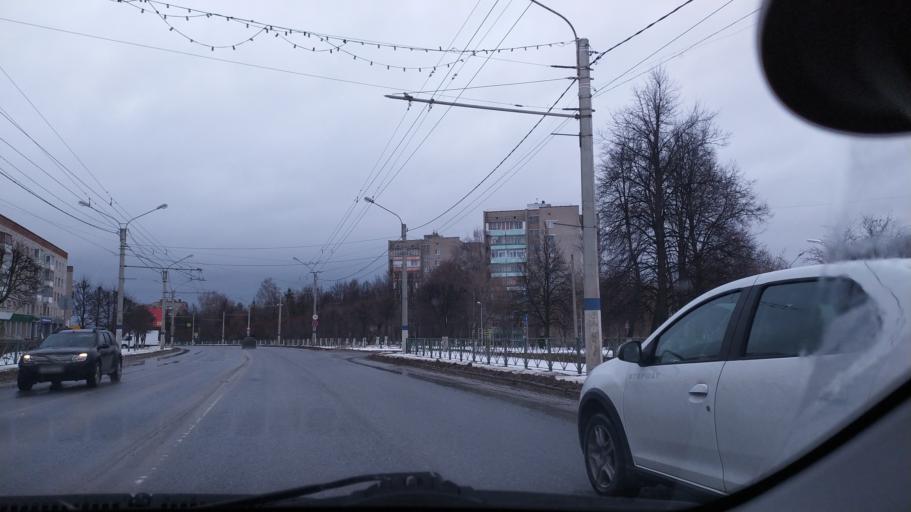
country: RU
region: Chuvashia
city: Novocheboksarsk
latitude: 56.1186
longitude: 47.4930
